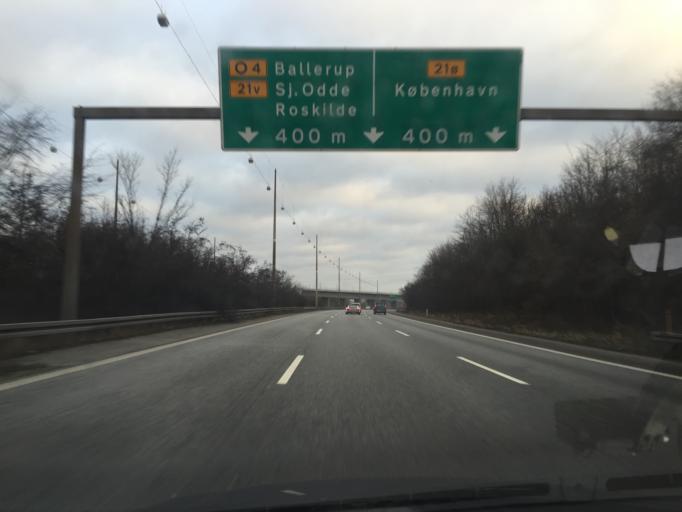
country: DK
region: Capital Region
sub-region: Ishoj Kommune
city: Ishoj
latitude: 55.6302
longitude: 12.3303
